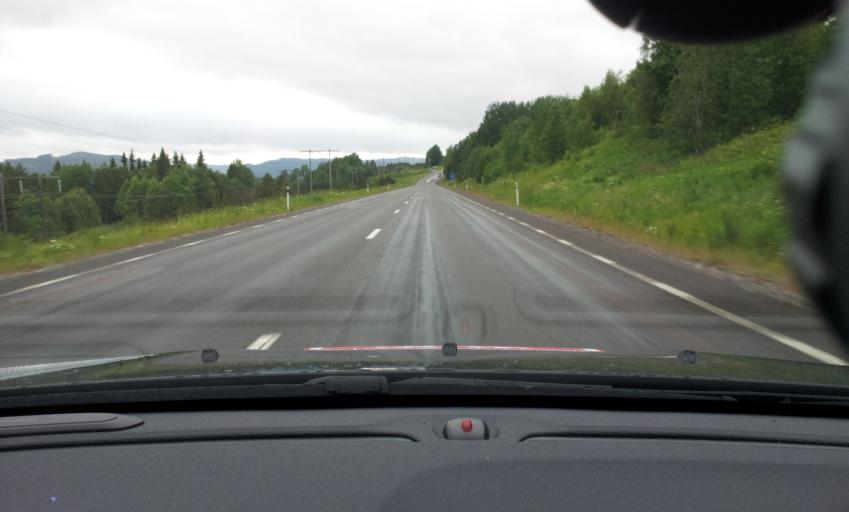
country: SE
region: Jaemtland
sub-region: Ragunda Kommun
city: Hammarstrand
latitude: 63.0499
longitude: 16.5307
